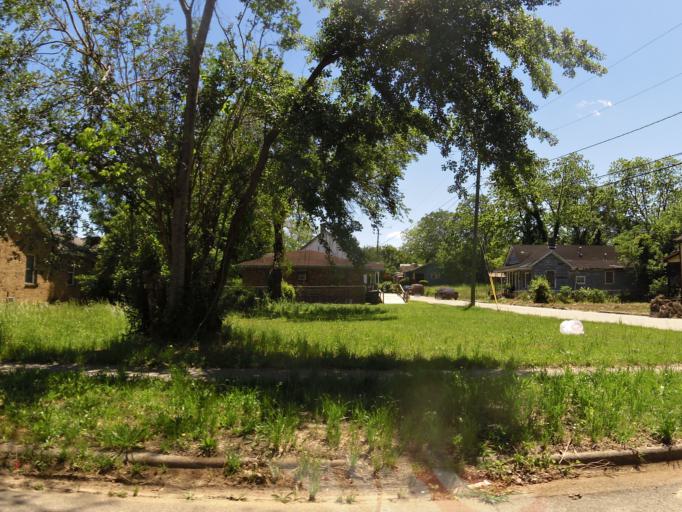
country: US
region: Georgia
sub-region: Richmond County
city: Augusta
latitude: 33.4595
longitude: -81.9791
